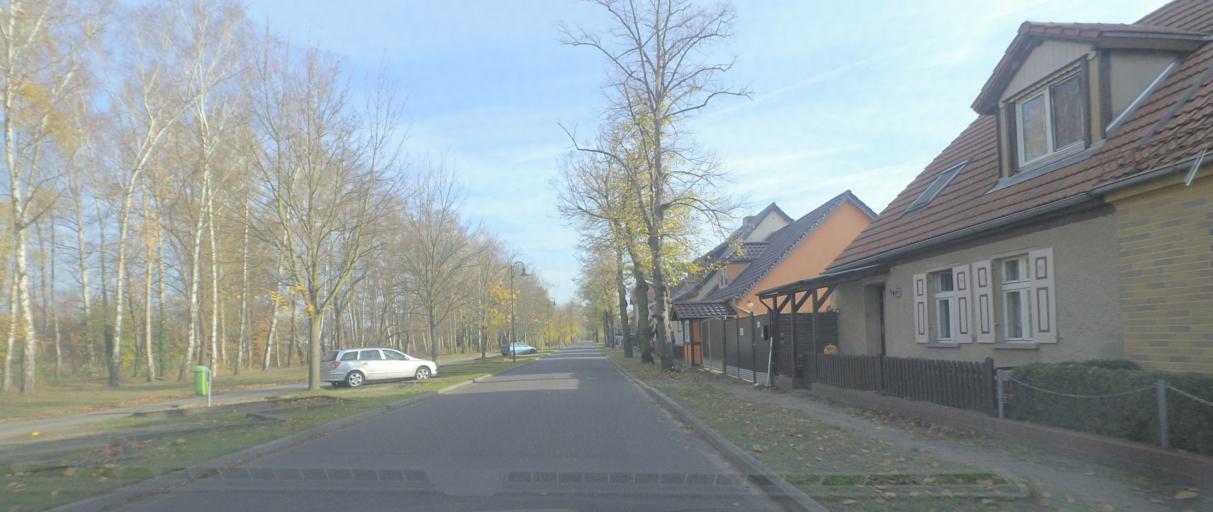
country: DE
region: Brandenburg
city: Sperenberg
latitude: 52.1353
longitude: 13.3705
